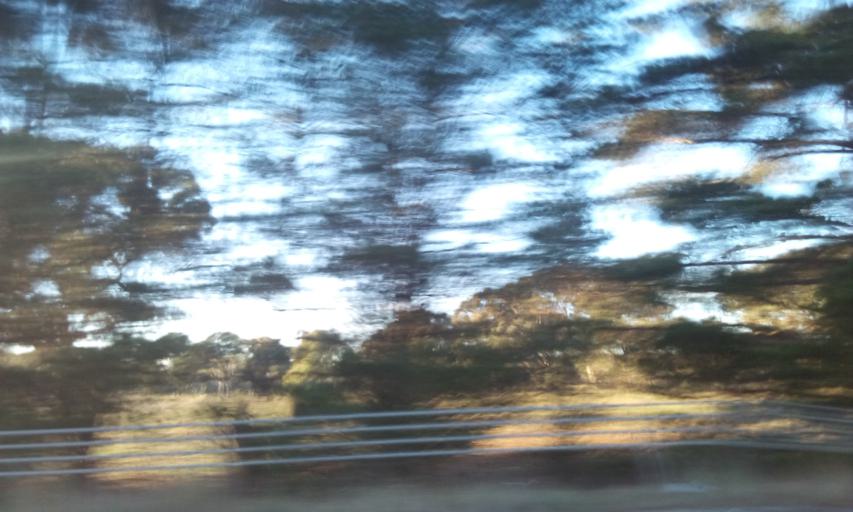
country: AU
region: New South Wales
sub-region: Goulburn Mulwaree
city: Goulburn
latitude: -34.8919
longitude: 149.5261
